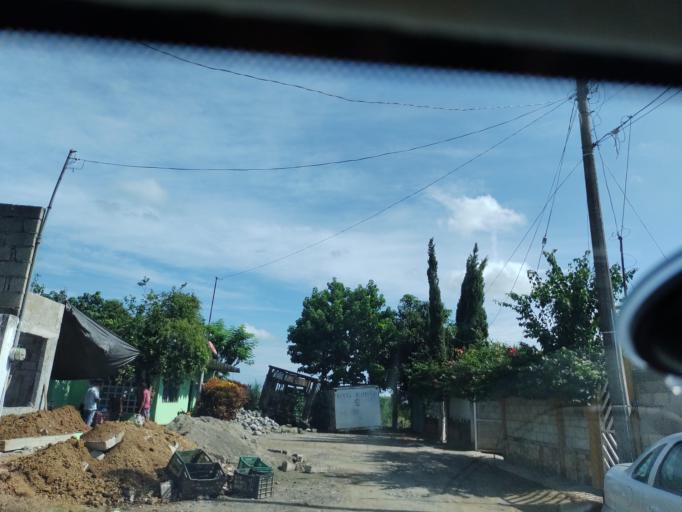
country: MX
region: Veracruz
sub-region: Martinez de la Torre
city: El Progreso
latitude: 20.1154
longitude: -97.0123
